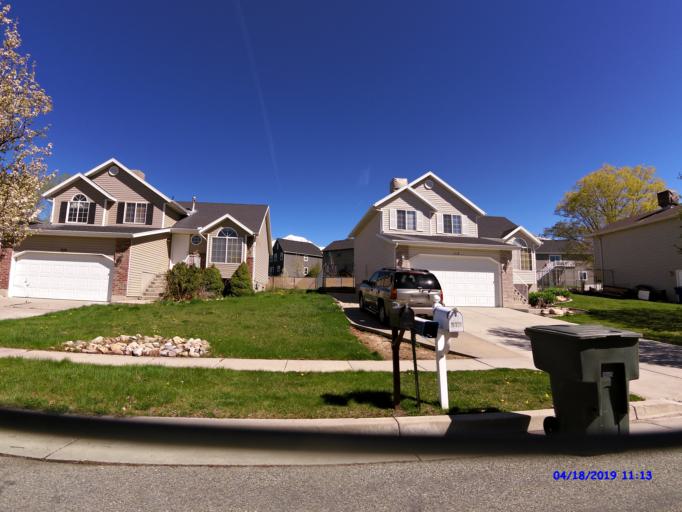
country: US
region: Utah
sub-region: Weber County
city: North Ogden
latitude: 41.2849
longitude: -111.9562
